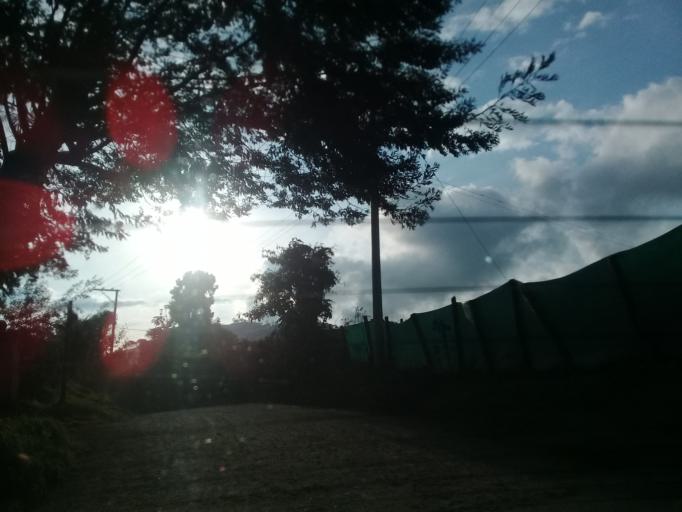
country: CO
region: Cundinamarca
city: Sibate
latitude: 4.4508
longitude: -74.2726
